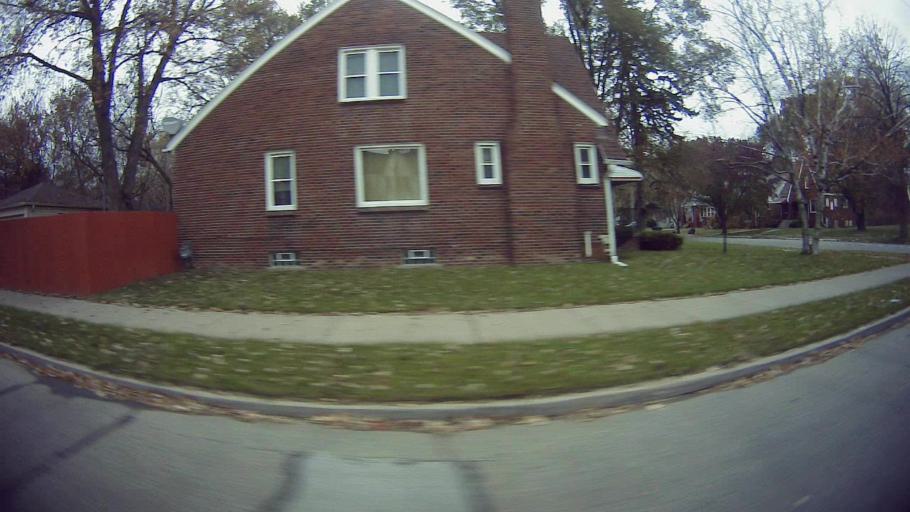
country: US
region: Michigan
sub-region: Macomb County
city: Eastpointe
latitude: 42.4325
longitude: -82.9850
